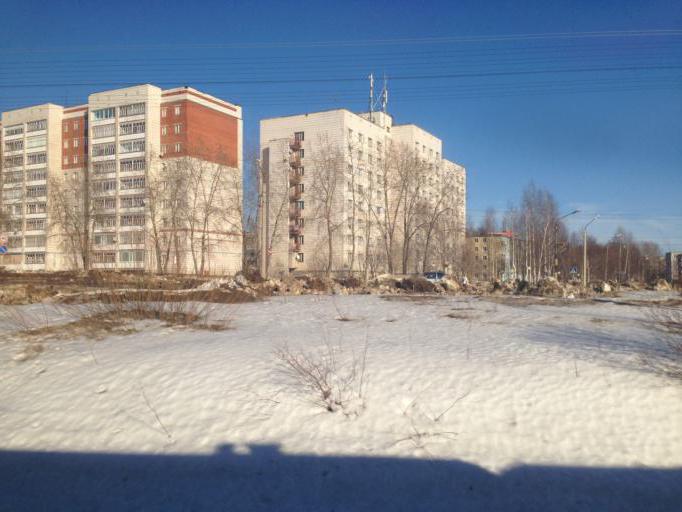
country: RU
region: Komi Republic
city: Ezhva
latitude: 61.7955
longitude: 50.7379
